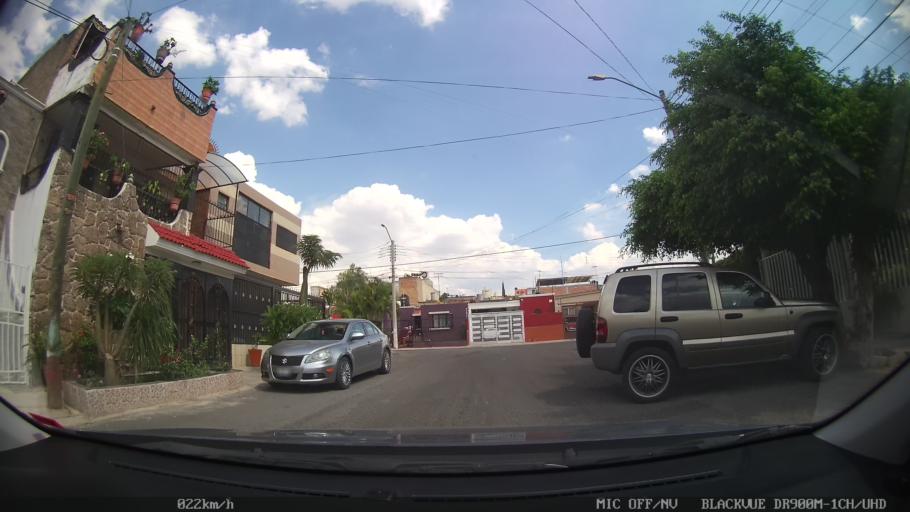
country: MX
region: Jalisco
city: Tlaquepaque
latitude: 20.6296
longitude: -103.2651
